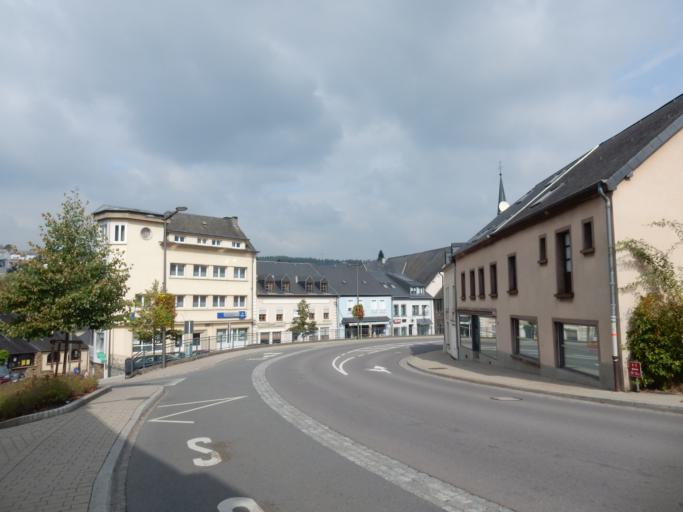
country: LU
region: Diekirch
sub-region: Canton de Wiltz
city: Wiltz
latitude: 49.9684
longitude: 5.9305
